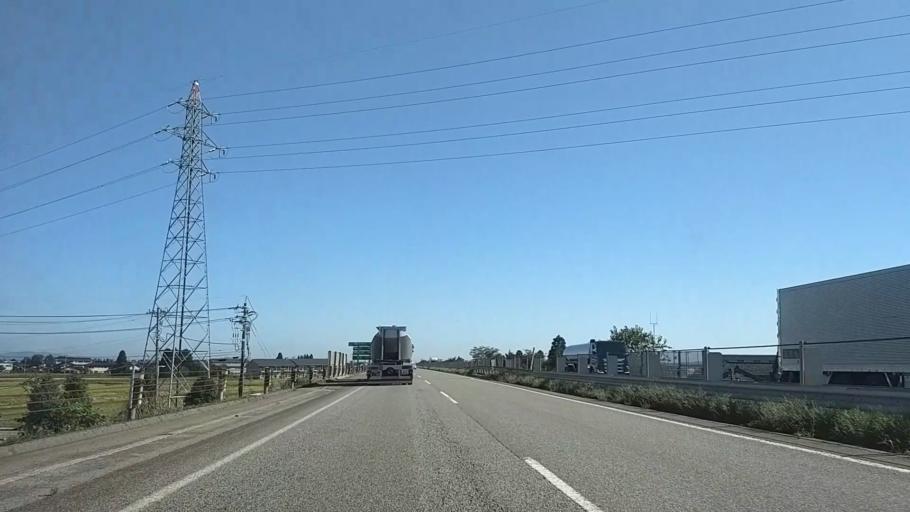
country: JP
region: Toyama
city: Nanto-shi
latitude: 36.6302
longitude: 136.9640
